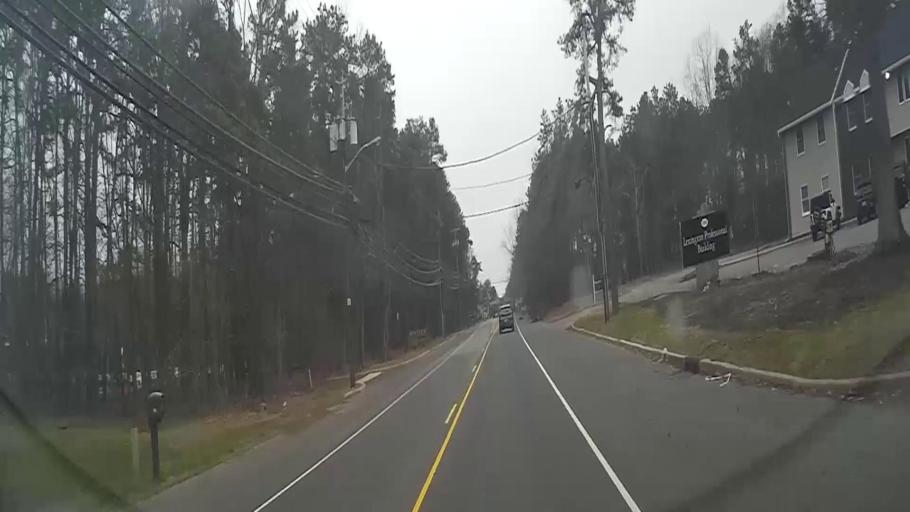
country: US
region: New Jersey
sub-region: Burlington County
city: Medford Lakes
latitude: 39.8723
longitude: -74.8483
